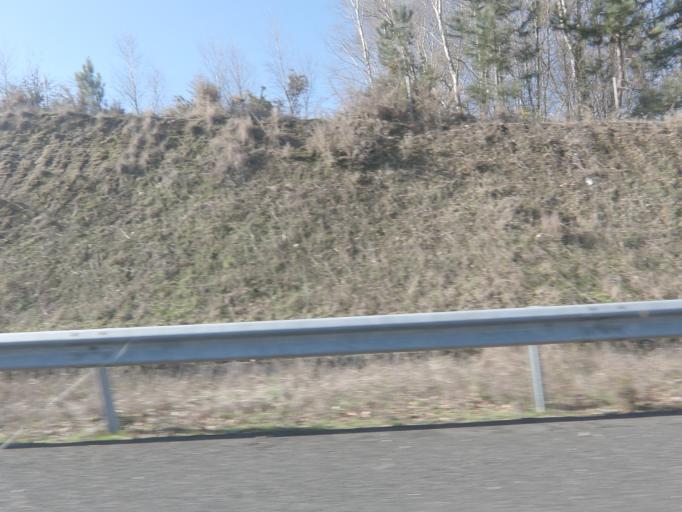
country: ES
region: Galicia
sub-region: Provincia de Pontevedra
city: Lalin
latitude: 42.6592
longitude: -8.1419
